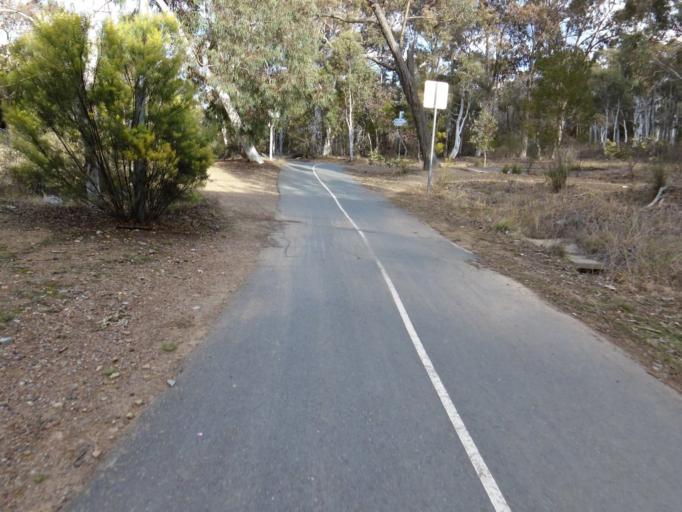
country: AU
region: Australian Capital Territory
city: Acton
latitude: -35.2514
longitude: 149.1067
